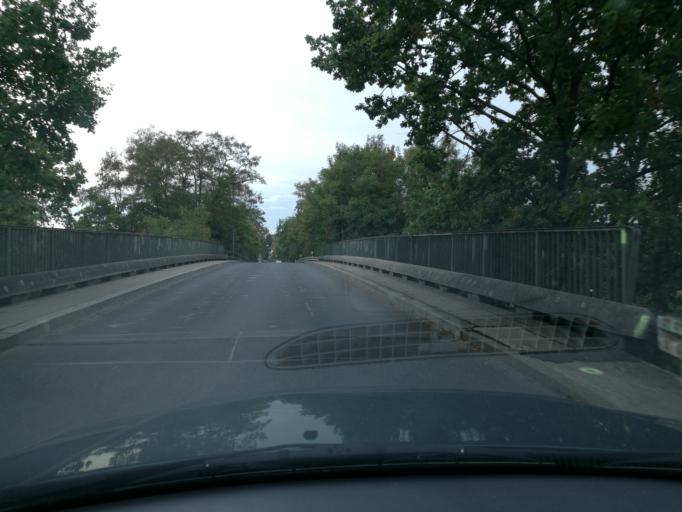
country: DE
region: Bavaria
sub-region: Regierungsbezirk Mittelfranken
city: Furth
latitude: 49.5080
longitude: 10.9842
